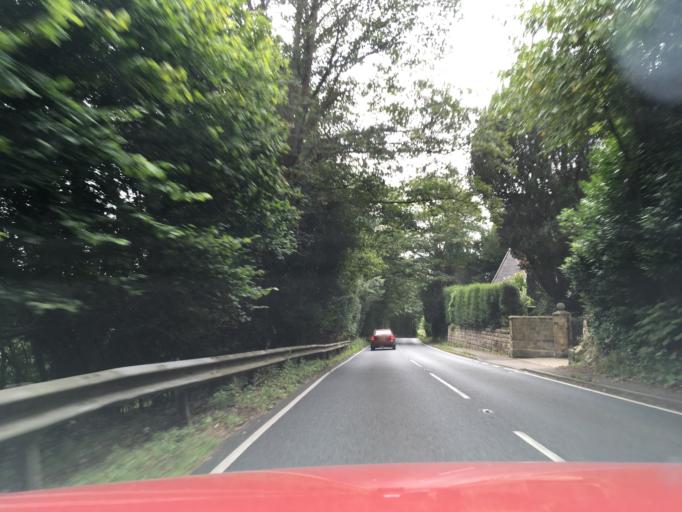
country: GB
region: England
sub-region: East Sussex
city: Crowborough
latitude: 51.1205
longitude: 0.1894
